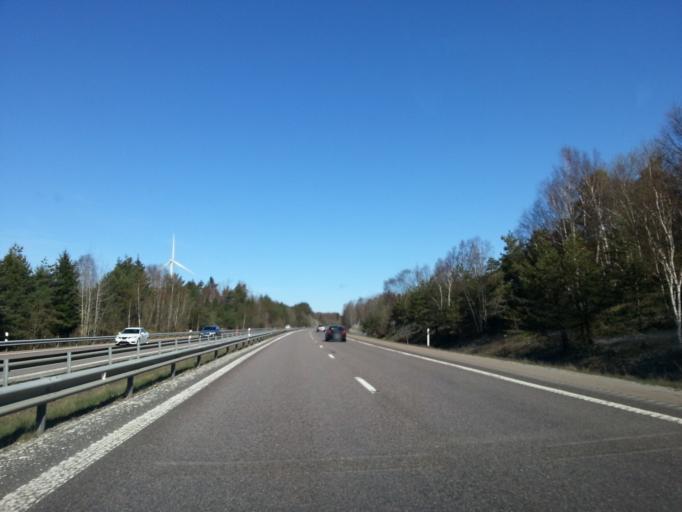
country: SE
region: Vaestra Goetaland
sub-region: Kungalvs Kommun
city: Kode
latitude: 57.9177
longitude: 11.8842
